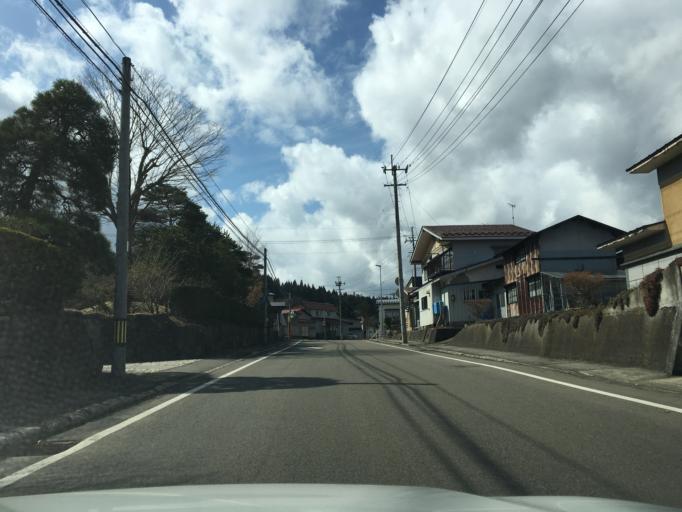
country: JP
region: Akita
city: Takanosu
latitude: 40.1192
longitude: 140.3709
